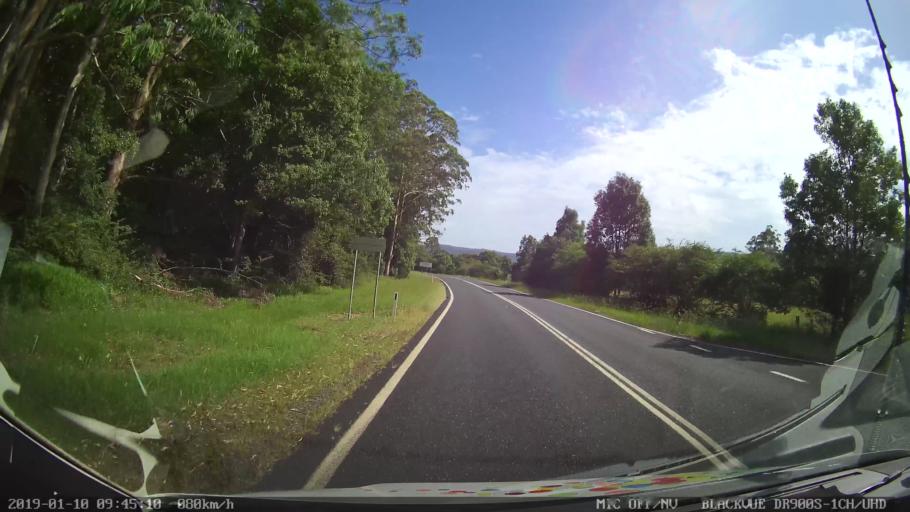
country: AU
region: New South Wales
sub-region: Coffs Harbour
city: Nana Glen
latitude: -30.1080
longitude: 153.0041
